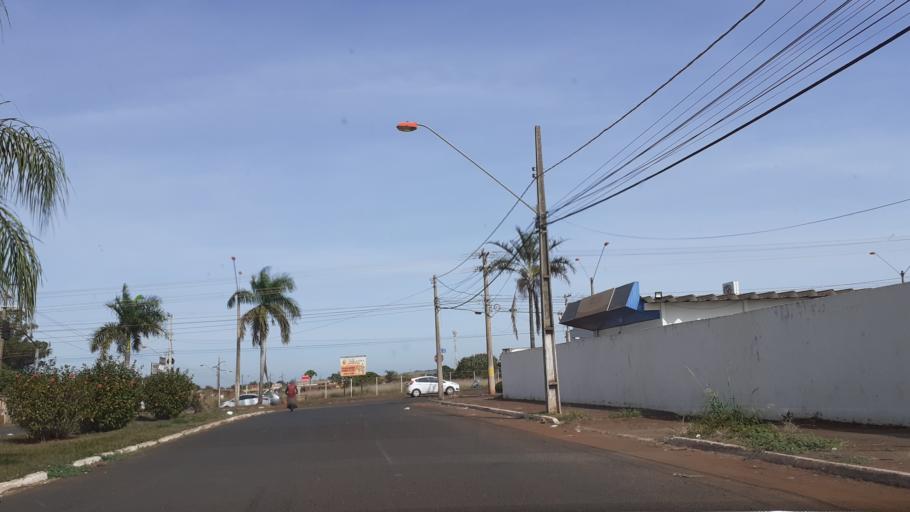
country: BR
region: Goias
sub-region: Itumbiara
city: Itumbiara
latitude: -18.4122
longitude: -49.2432
